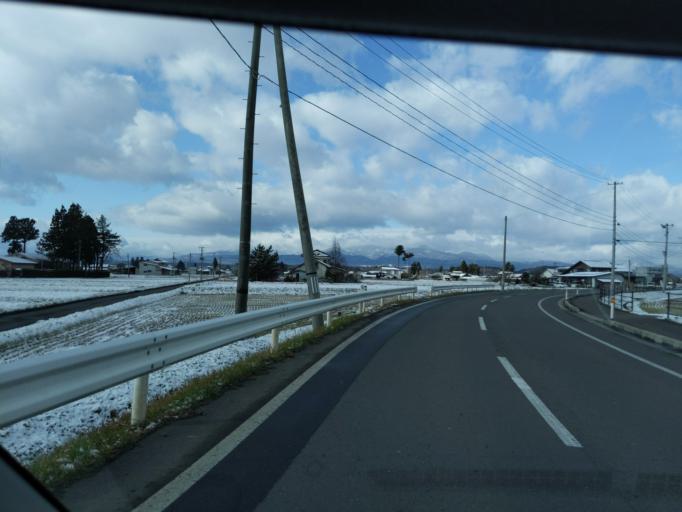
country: JP
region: Iwate
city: Mizusawa
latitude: 39.1623
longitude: 141.1064
